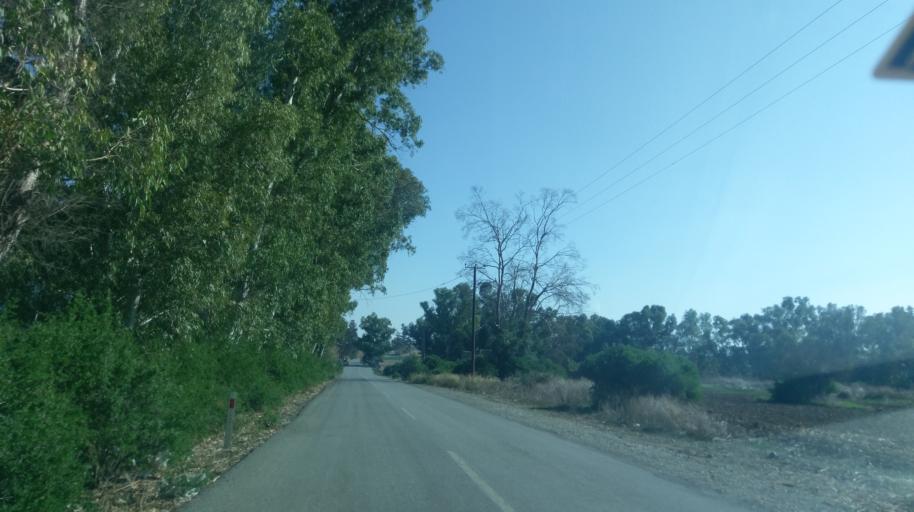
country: CY
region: Larnaka
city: Athienou
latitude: 35.0822
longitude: 33.4859
